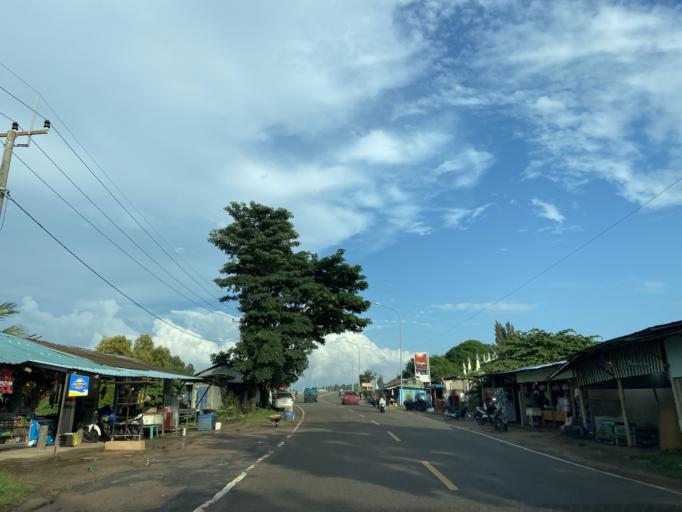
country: SG
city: Singapore
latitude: 0.9761
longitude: 104.0525
